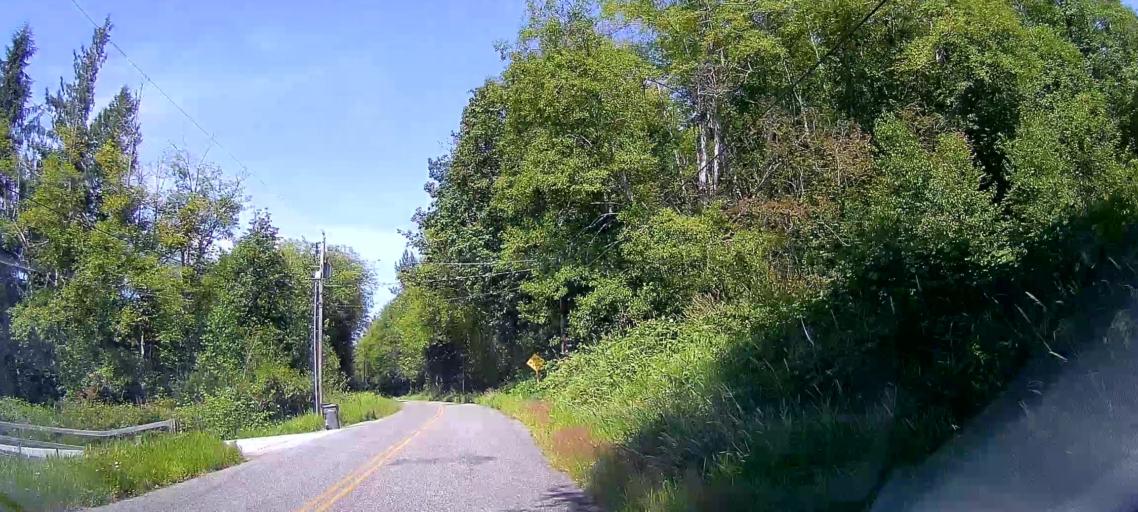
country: US
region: Washington
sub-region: Whatcom County
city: Sudden Valley
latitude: 48.6090
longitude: -122.3180
